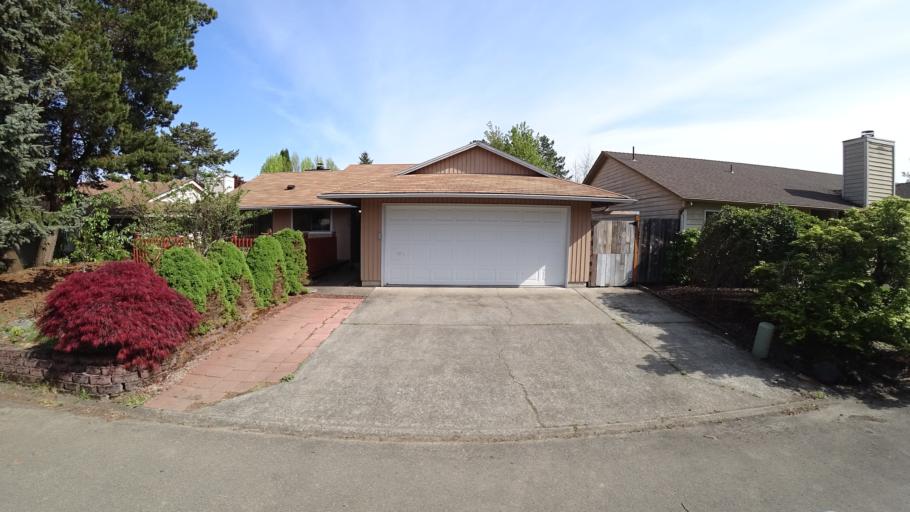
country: US
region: Oregon
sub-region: Washington County
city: Hillsboro
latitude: 45.5251
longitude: -122.9560
